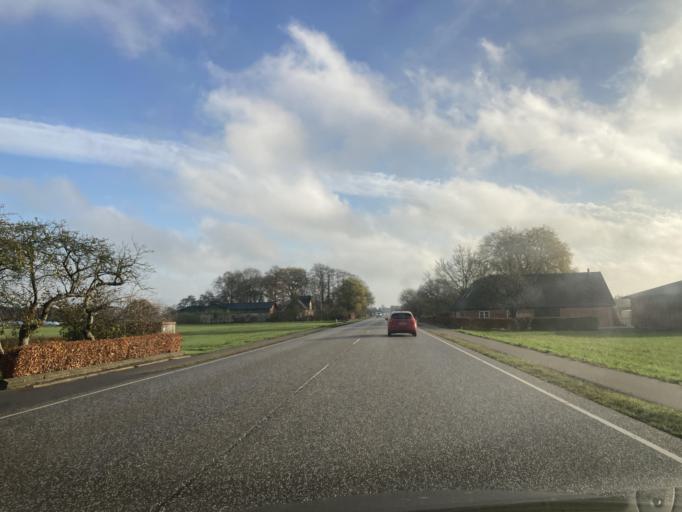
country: DK
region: Zealand
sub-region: Guldborgsund Kommune
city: Sundby
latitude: 54.7752
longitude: 11.7335
